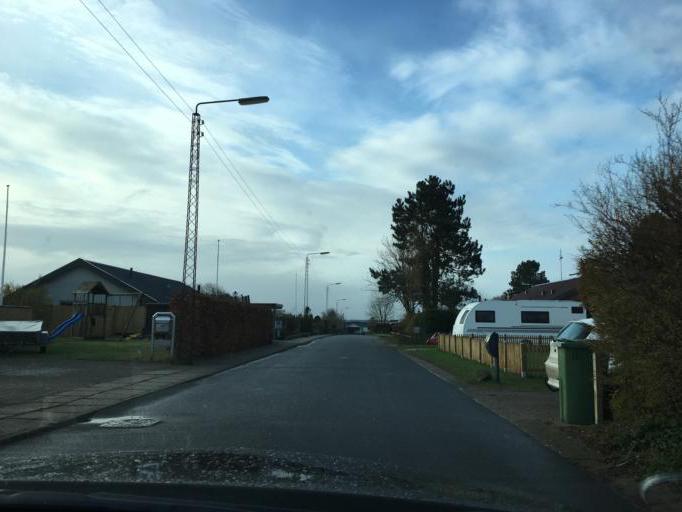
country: DK
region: South Denmark
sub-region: Kolding Kommune
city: Kolding
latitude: 55.5661
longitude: 9.4849
